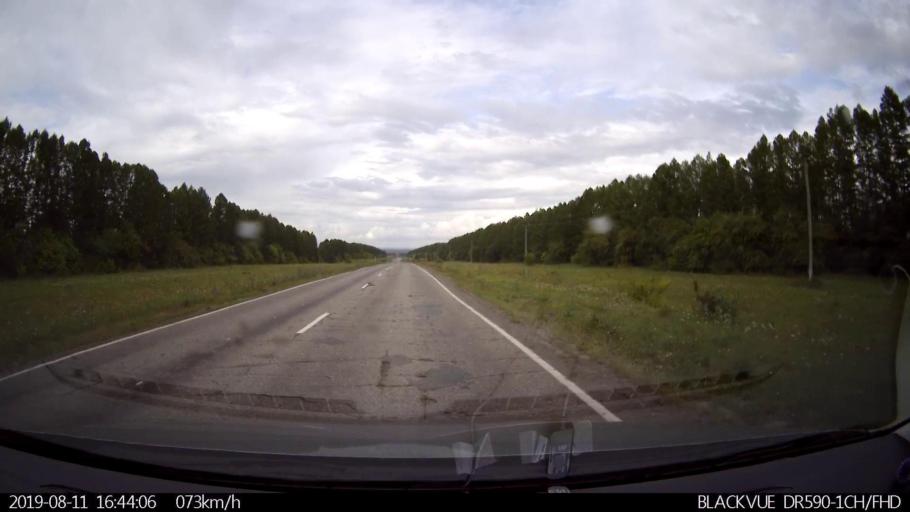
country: RU
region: Ulyanovsk
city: Mayna
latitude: 54.1758
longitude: 47.6780
